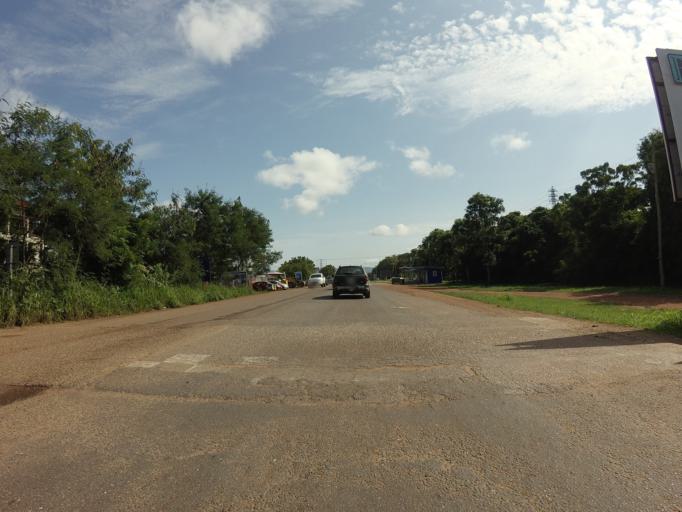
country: GH
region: Eastern
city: Aburi
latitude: 5.7981
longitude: -0.1276
